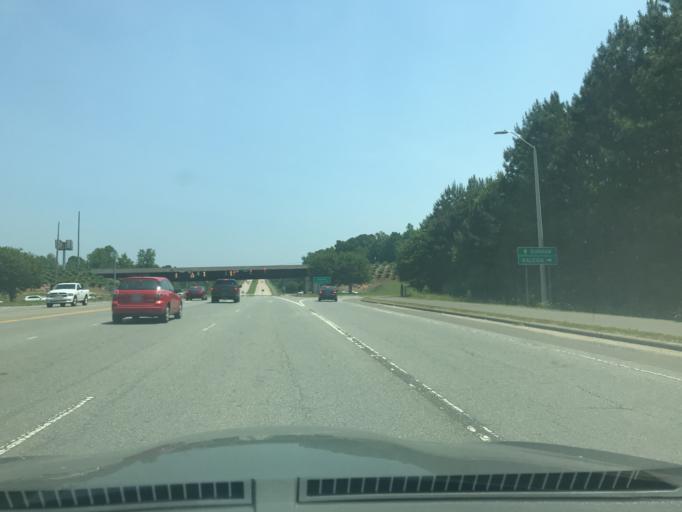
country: US
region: North Carolina
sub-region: Wake County
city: Cary
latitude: 35.8062
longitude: -78.7245
